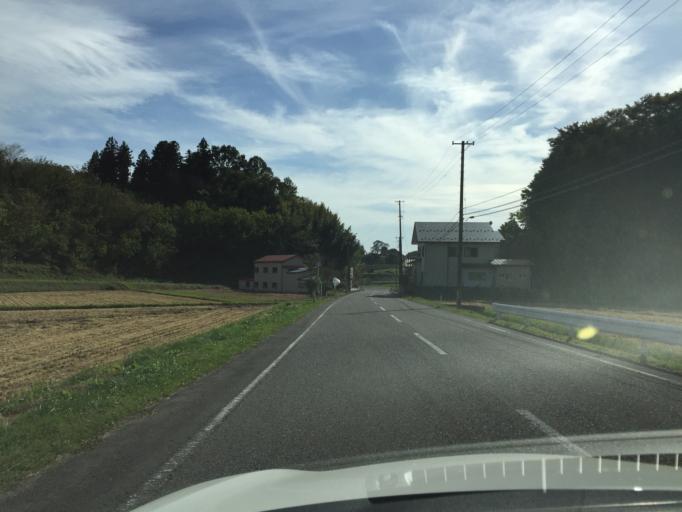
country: JP
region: Fukushima
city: Miharu
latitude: 37.4707
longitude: 140.4929
